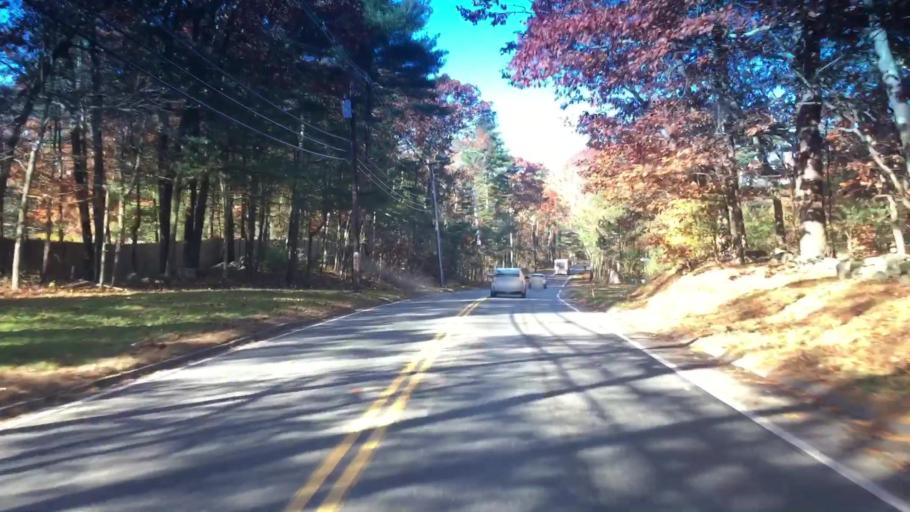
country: US
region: Massachusetts
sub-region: Norfolk County
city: Medfield
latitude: 42.1660
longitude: -71.2901
